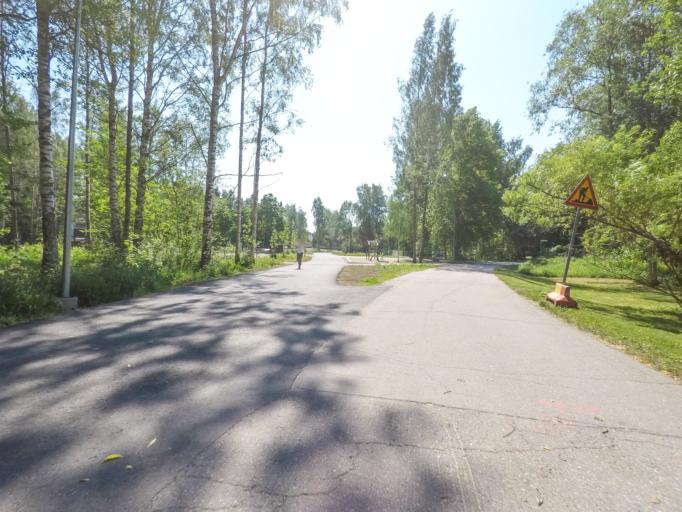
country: FI
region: Uusimaa
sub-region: Helsinki
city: Vantaa
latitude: 60.2146
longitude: 25.1406
